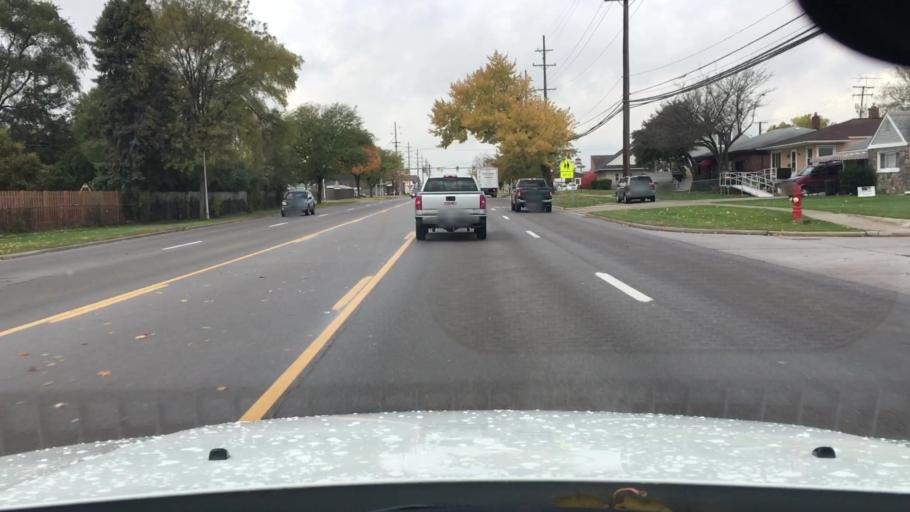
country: US
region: Michigan
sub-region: Oakland County
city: Madison Heights
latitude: 42.5050
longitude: -83.0977
